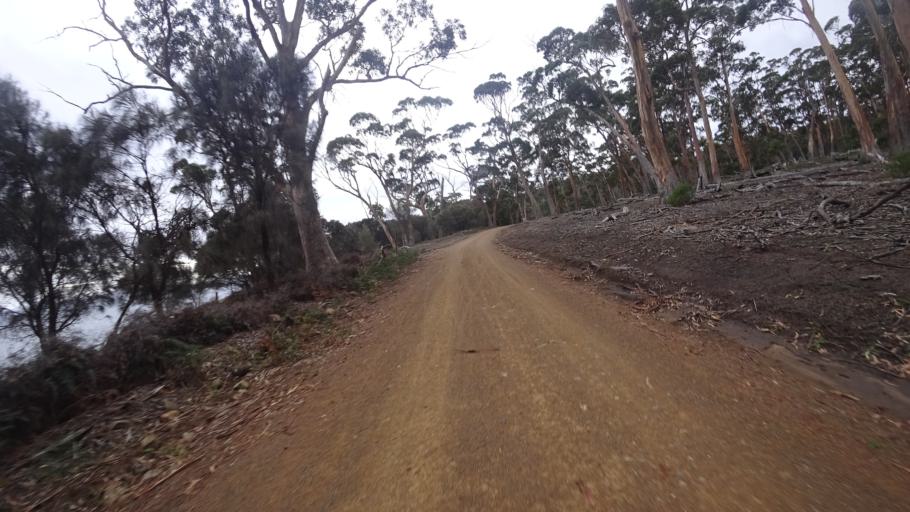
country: AU
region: Tasmania
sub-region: Sorell
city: Sorell
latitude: -42.6092
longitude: 148.0469
